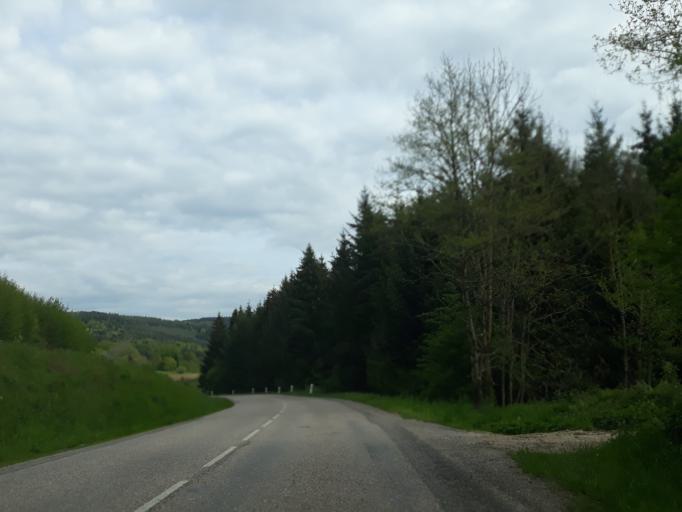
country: FR
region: Lorraine
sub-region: Departement des Vosges
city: Granges-sur-Vologne
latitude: 48.1754
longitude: 6.7669
